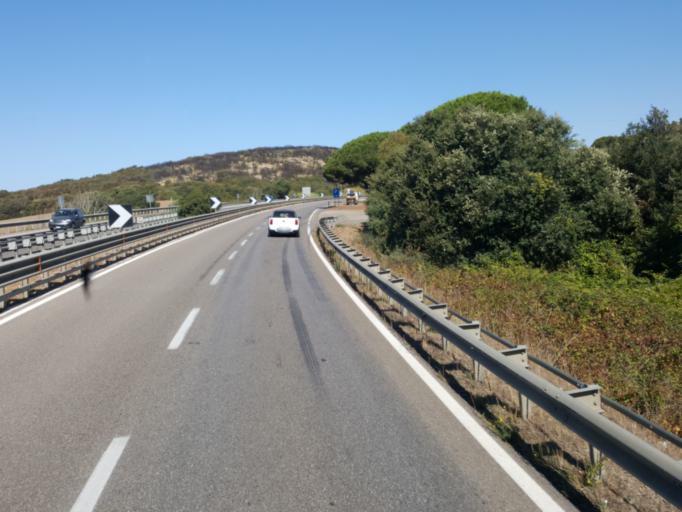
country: IT
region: Tuscany
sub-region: Provincia di Grosseto
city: Orbetello Scalo
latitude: 42.4198
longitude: 11.2923
